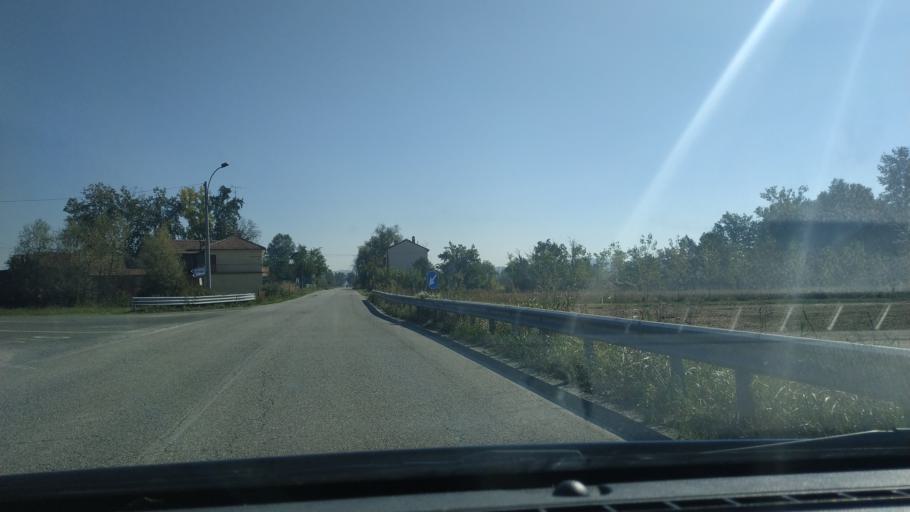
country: IT
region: Piedmont
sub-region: Provincia di Alessandria
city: Serralunga di Crea
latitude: 45.1134
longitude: 8.2982
